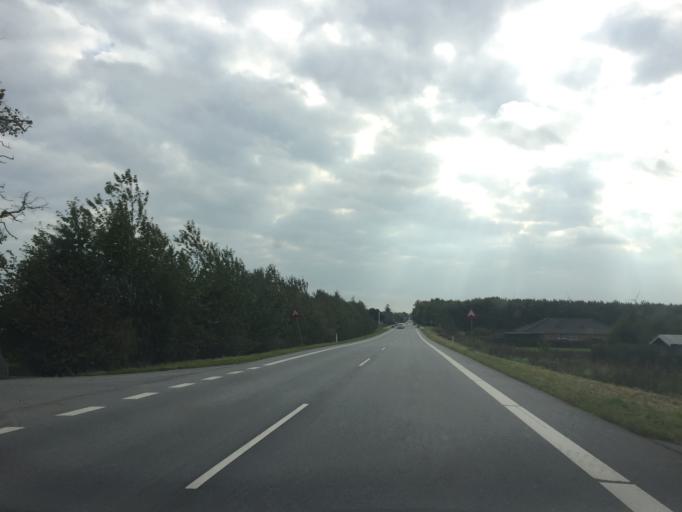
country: DK
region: Zealand
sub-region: Faxe Kommune
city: Ronnede
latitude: 55.1743
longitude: 11.9828
